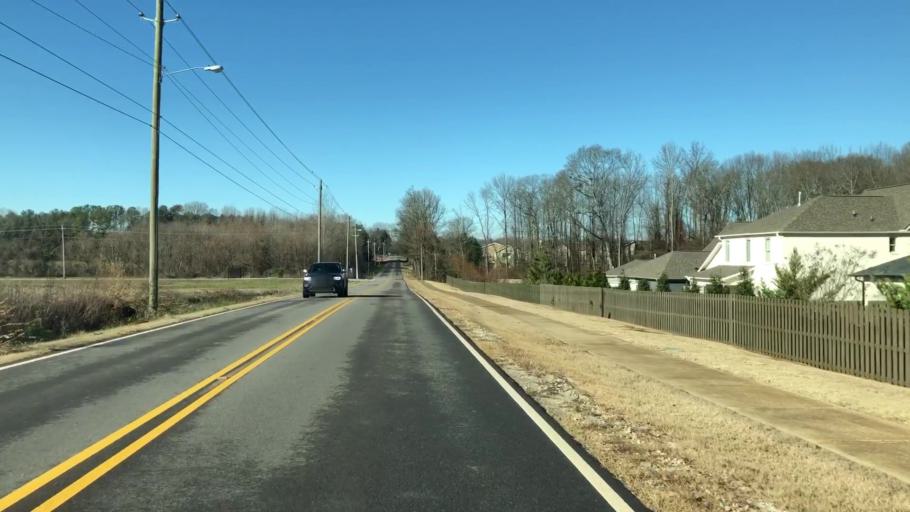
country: US
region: Alabama
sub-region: Madison County
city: Madison
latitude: 34.6923
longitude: -86.7777
